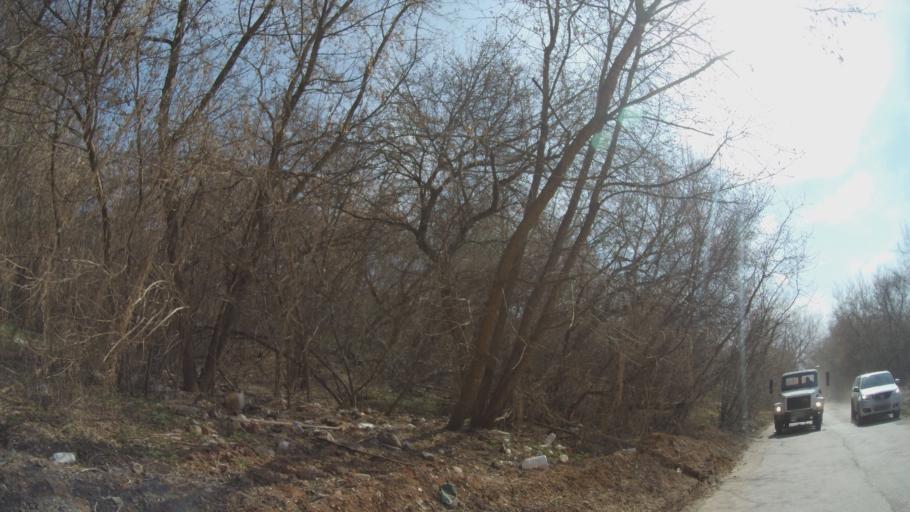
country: RU
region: Nizjnij Novgorod
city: Vyyezdnoye
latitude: 55.3897
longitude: 43.8091
